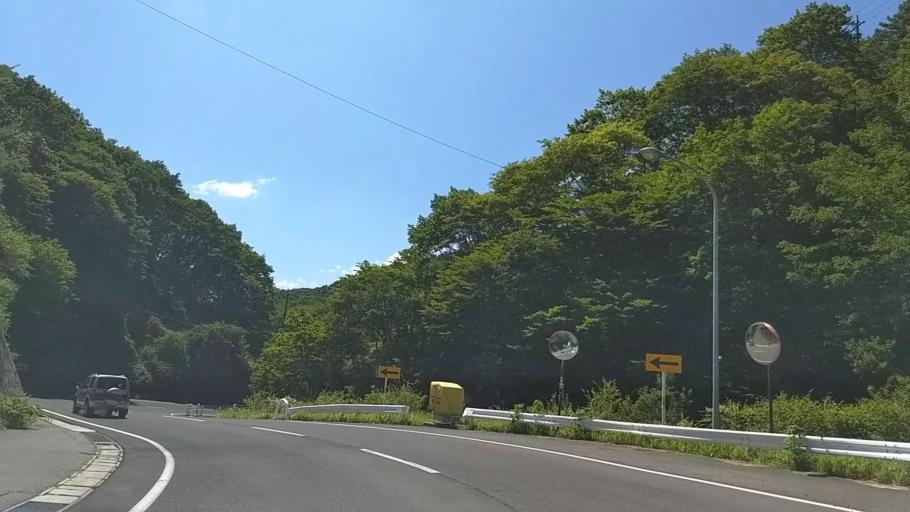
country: JP
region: Nagano
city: Chino
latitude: 36.0982
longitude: 138.2248
